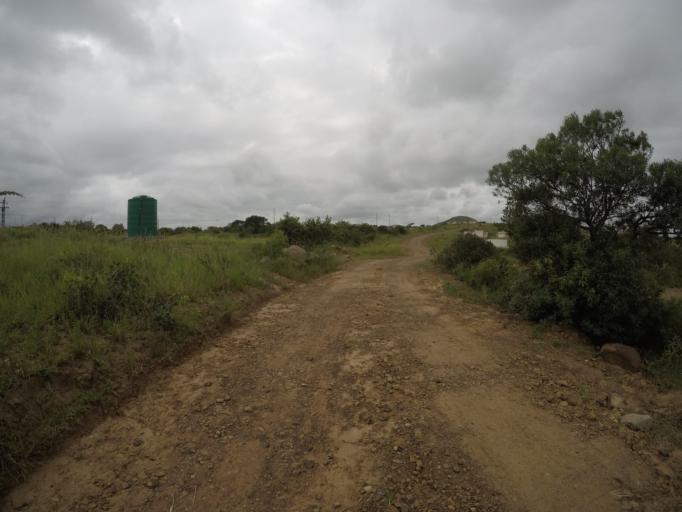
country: ZA
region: KwaZulu-Natal
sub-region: uThungulu District Municipality
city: Empangeni
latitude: -28.6034
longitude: 31.8387
